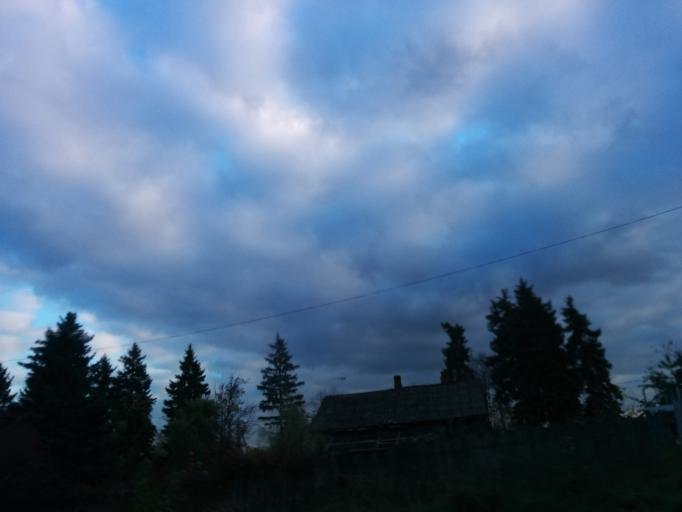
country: RU
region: Moscow
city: Annino
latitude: 55.5442
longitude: 37.6013
